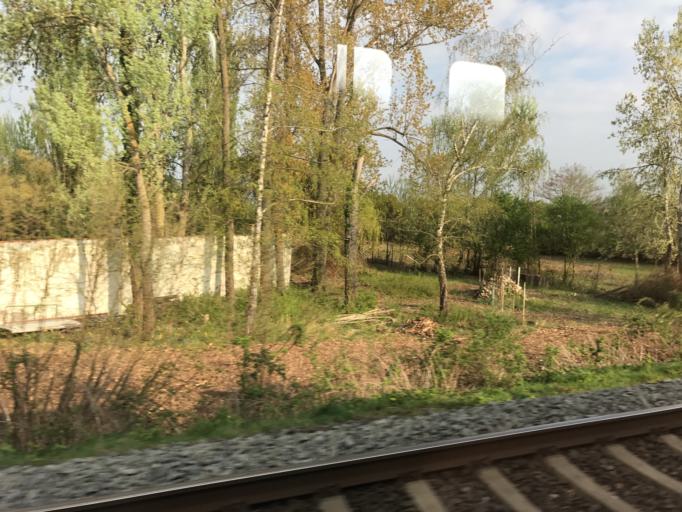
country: DE
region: Rheinland-Pfalz
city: Osthofen
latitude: 49.7190
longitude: 8.3273
